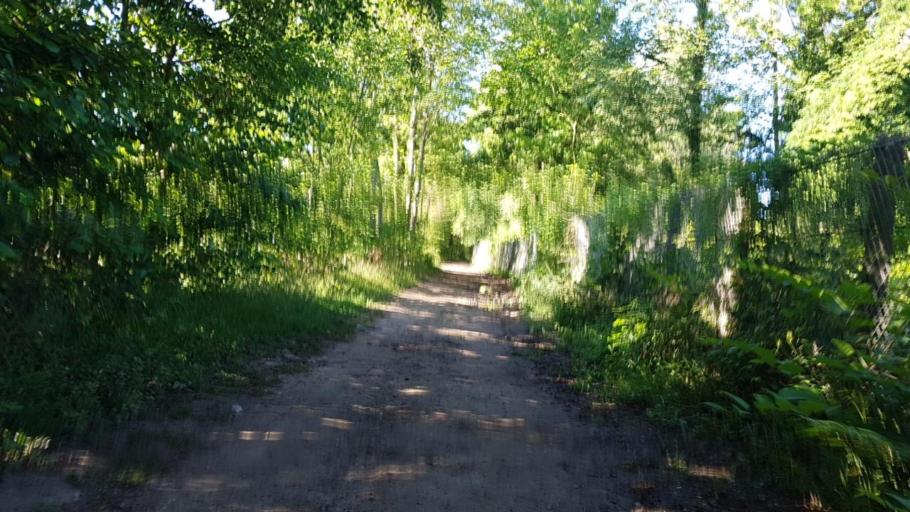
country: FR
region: Picardie
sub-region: Departement de l'Aisne
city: Essomes-sur-Marne
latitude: 49.0268
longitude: 3.3805
